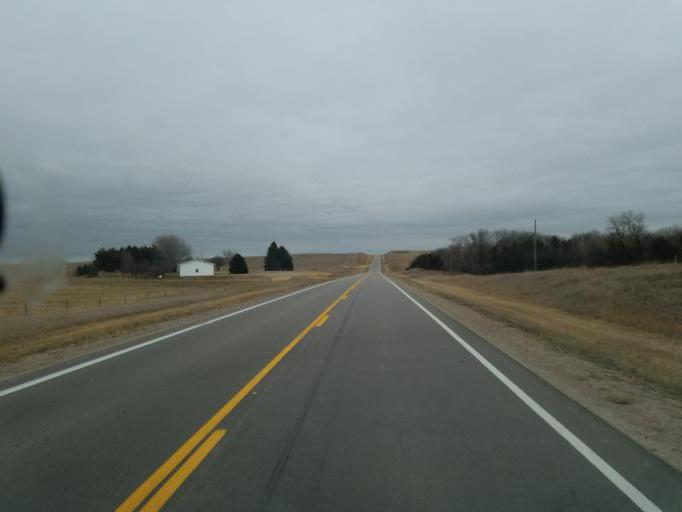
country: US
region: Nebraska
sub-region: Cedar County
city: Hartington
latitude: 42.6129
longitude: -97.4056
